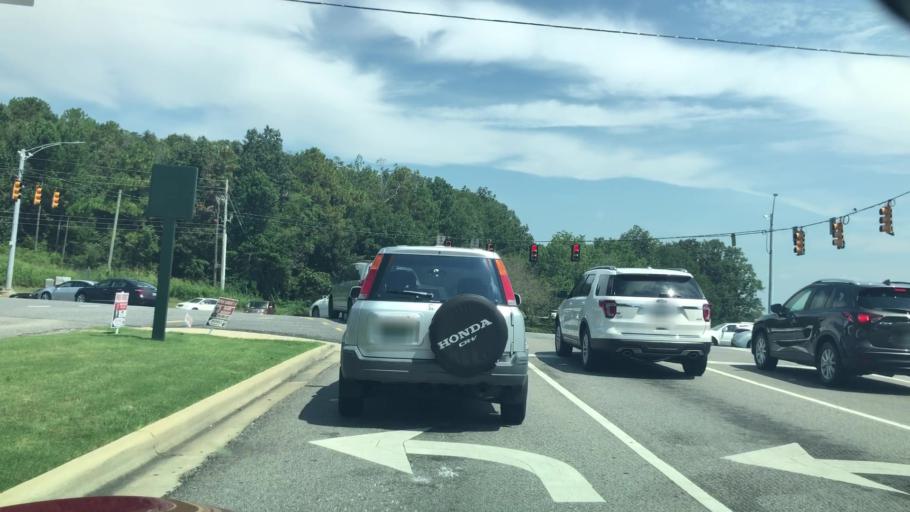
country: US
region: Alabama
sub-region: Shelby County
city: Lake Purdy
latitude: 33.4177
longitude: -86.6874
